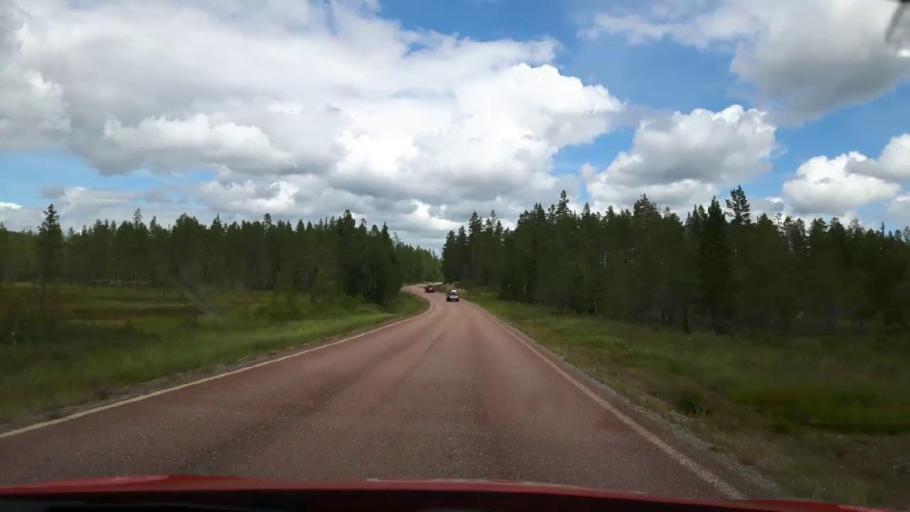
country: NO
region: Hedmark
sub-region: Trysil
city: Innbygda
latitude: 61.8991
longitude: 12.9892
